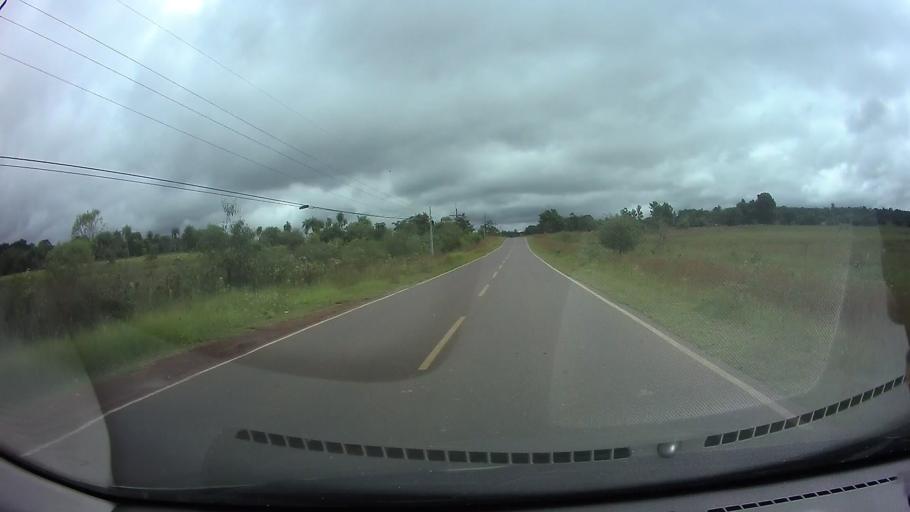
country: PY
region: Cordillera
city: Atyra
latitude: -25.2849
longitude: -57.1919
